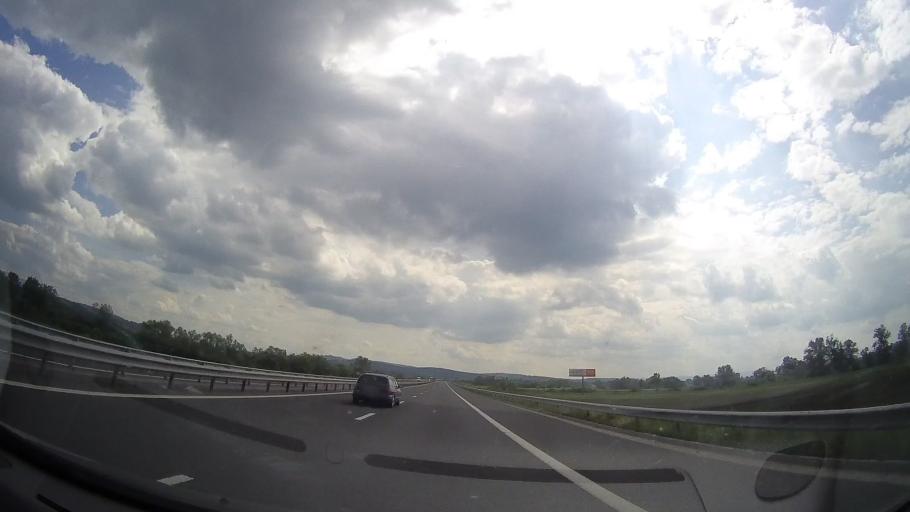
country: RO
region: Hunedoara
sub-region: Comuna Turdas
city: Pricaz
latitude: 45.8649
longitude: 23.1537
